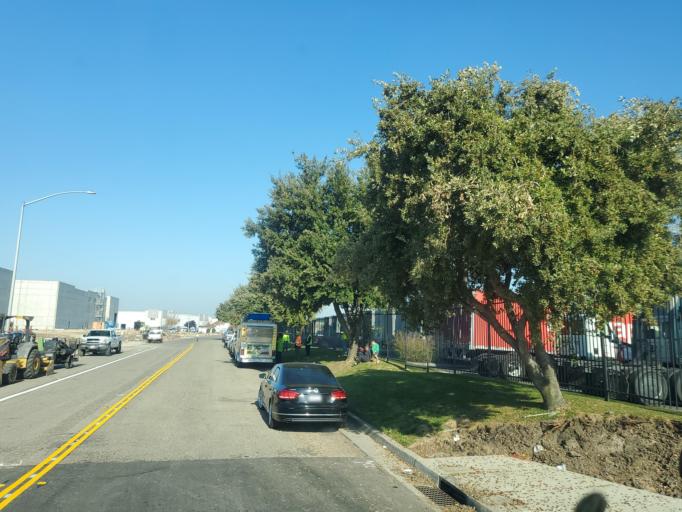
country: US
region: California
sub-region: San Joaquin County
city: Kennedy
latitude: 37.9046
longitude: -121.2486
